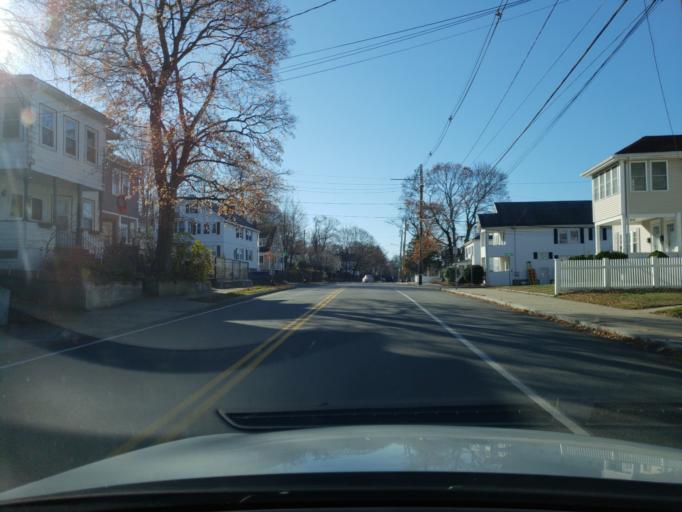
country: US
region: Massachusetts
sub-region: Middlesex County
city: Winchester
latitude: 42.4630
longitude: -71.1271
